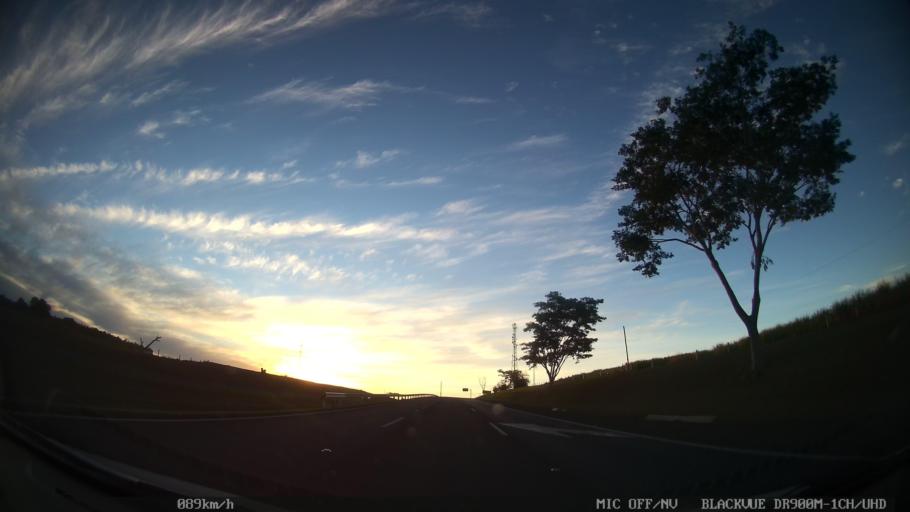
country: BR
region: Sao Paulo
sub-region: Pindorama
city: Pindorama
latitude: -21.2119
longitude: -48.9284
